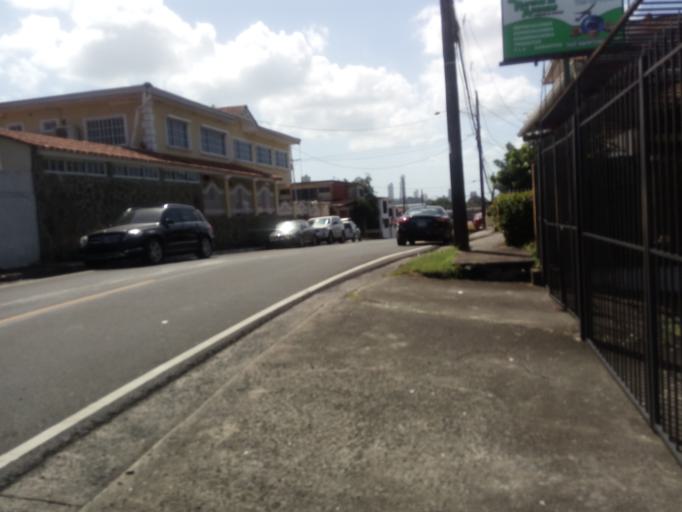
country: PA
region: Panama
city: Panama
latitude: 8.9956
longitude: -79.5380
